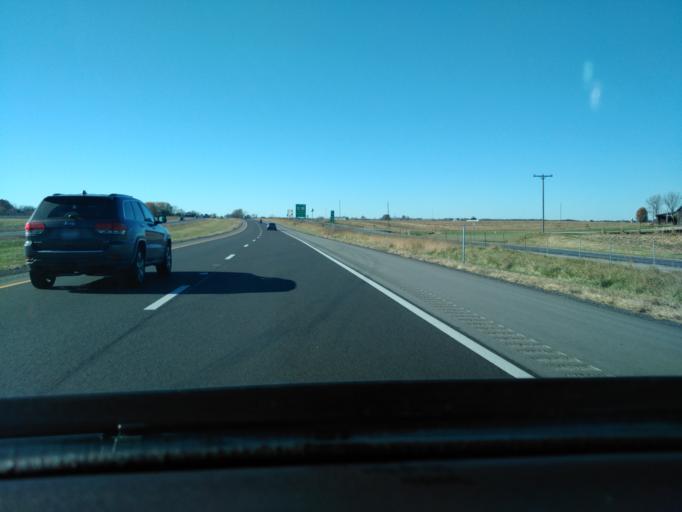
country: US
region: Illinois
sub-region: Madison County
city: Highland
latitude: 38.7930
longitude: -89.6150
